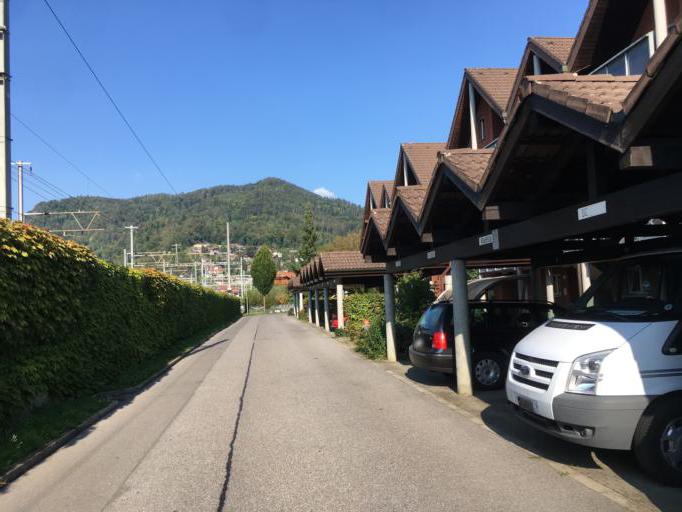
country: CH
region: Bern
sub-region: Thun District
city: Thun
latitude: 46.7467
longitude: 7.6306
